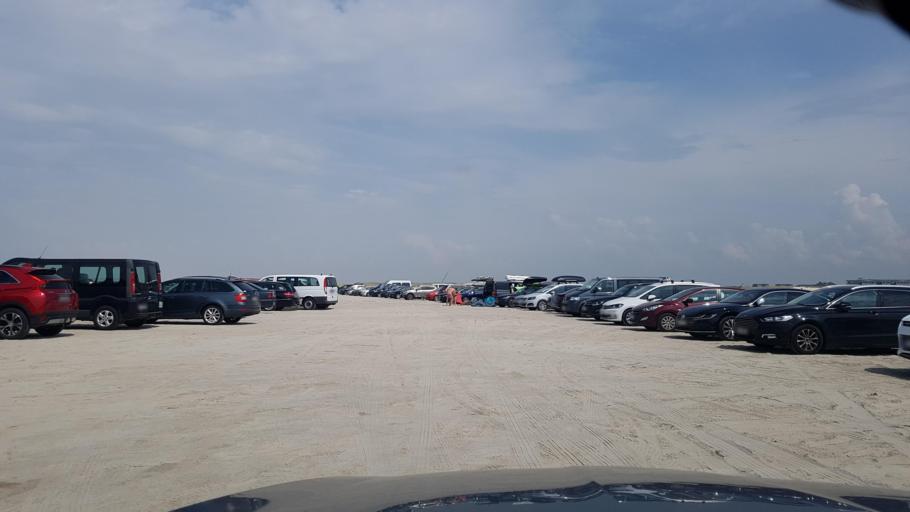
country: DE
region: Schleswig-Holstein
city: Sankt Peter-Ording
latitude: 54.3338
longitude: 8.5956
